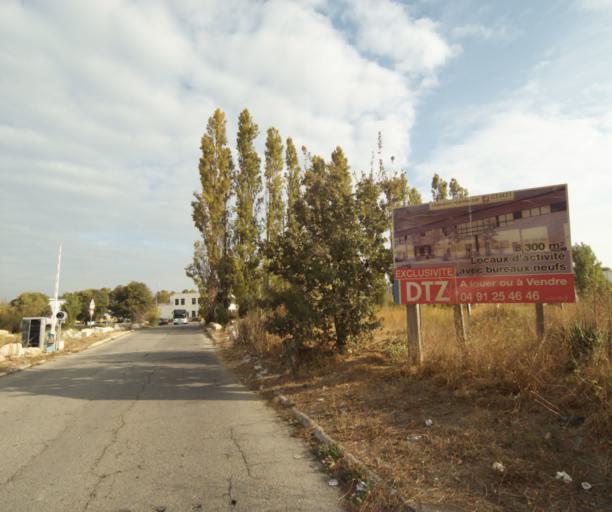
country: FR
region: Provence-Alpes-Cote d'Azur
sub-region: Departement des Bouches-du-Rhone
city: Saint-Victoret
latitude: 43.4210
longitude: 5.2598
